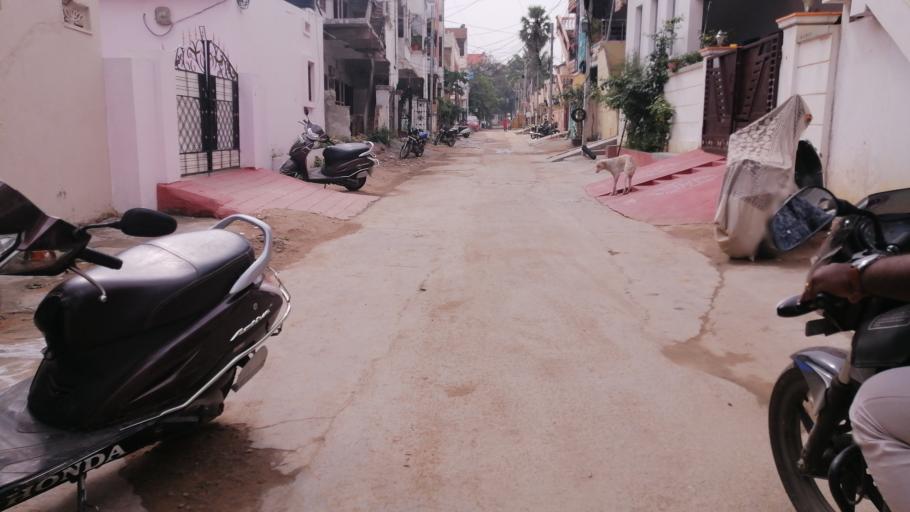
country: IN
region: Telangana
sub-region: Rangareddi
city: Secunderabad
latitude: 17.4832
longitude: 78.5812
